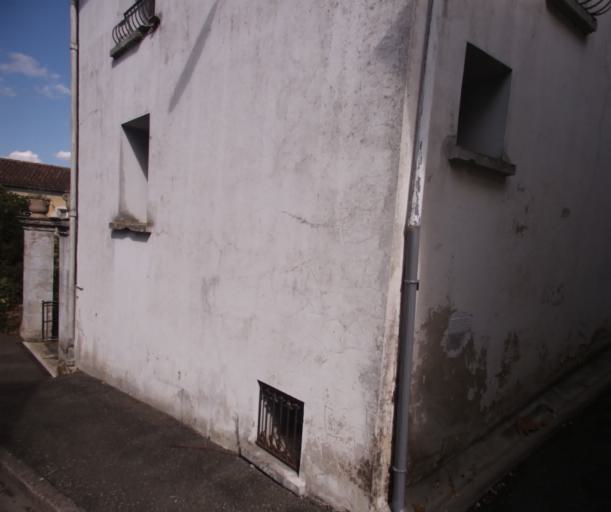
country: FR
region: Midi-Pyrenees
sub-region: Departement du Gers
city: Cazaubon
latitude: 43.9341
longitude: -0.0718
